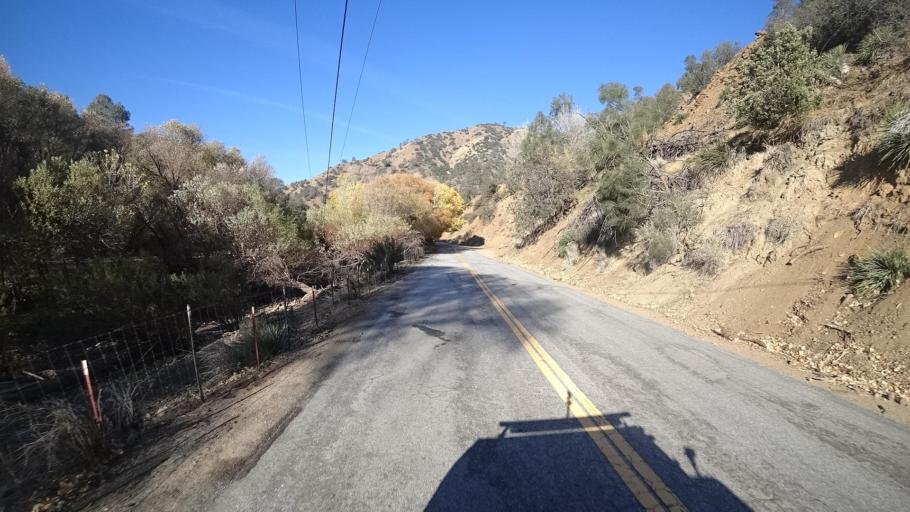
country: US
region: California
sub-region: Kern County
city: Golden Hills
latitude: 35.3033
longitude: -118.4572
